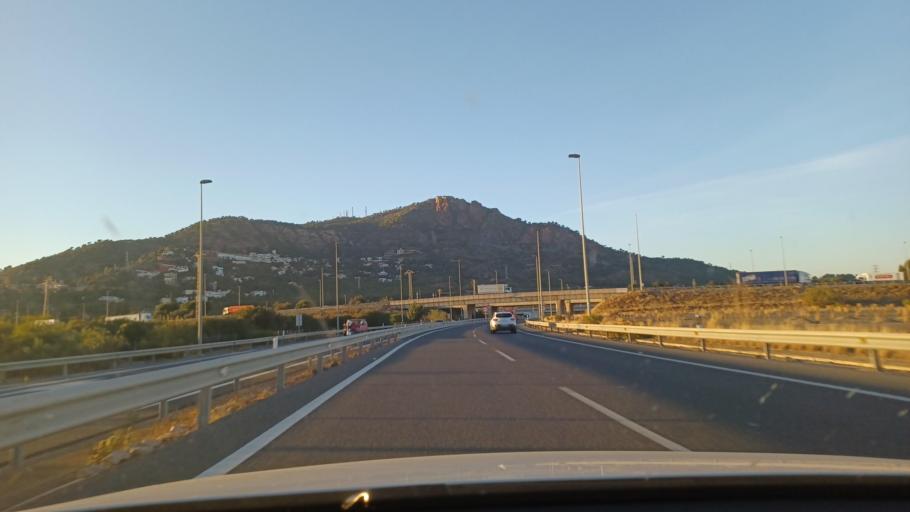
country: ES
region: Valencia
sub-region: Provincia de Valencia
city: Pucol
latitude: 39.6309
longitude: -0.3021
